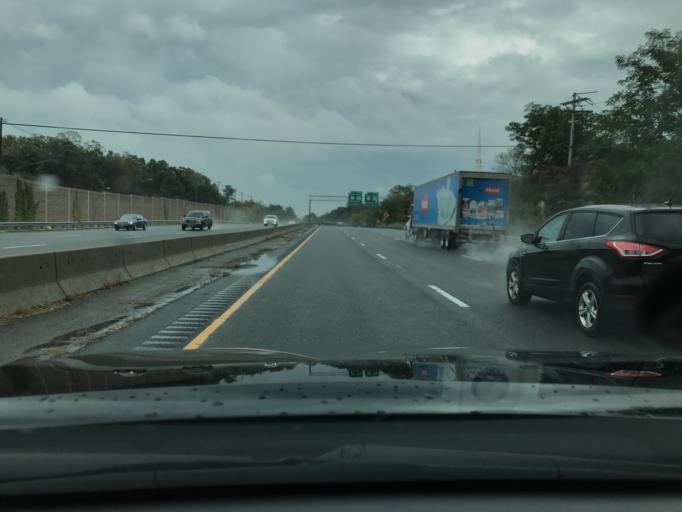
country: US
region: Massachusetts
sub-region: Essex County
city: Lynnfield
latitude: 42.5163
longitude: -71.0071
